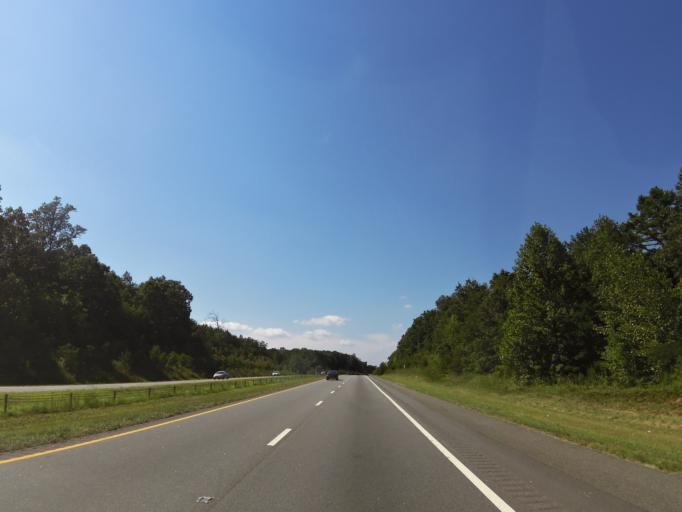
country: US
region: North Carolina
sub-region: Catawba County
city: Mountain View
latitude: 35.6470
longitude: -81.3075
